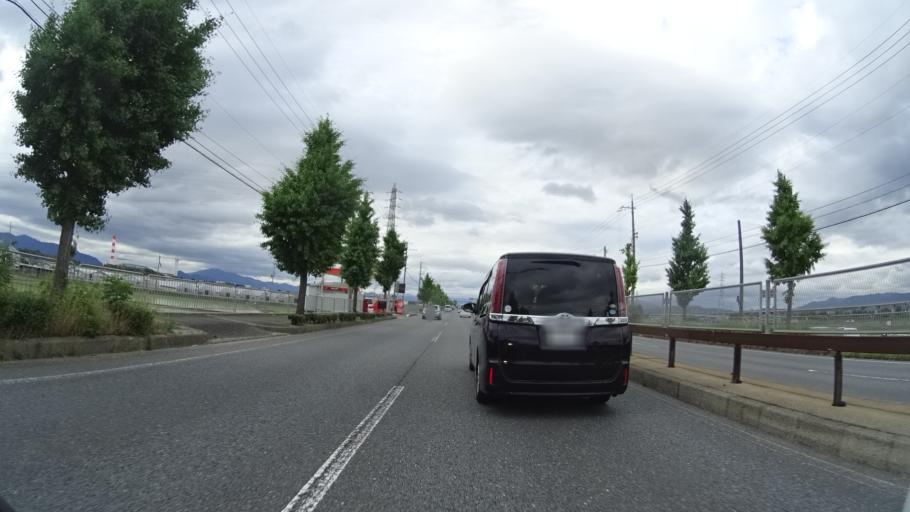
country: JP
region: Kyoto
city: Yawata
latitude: 34.9084
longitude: 135.7443
